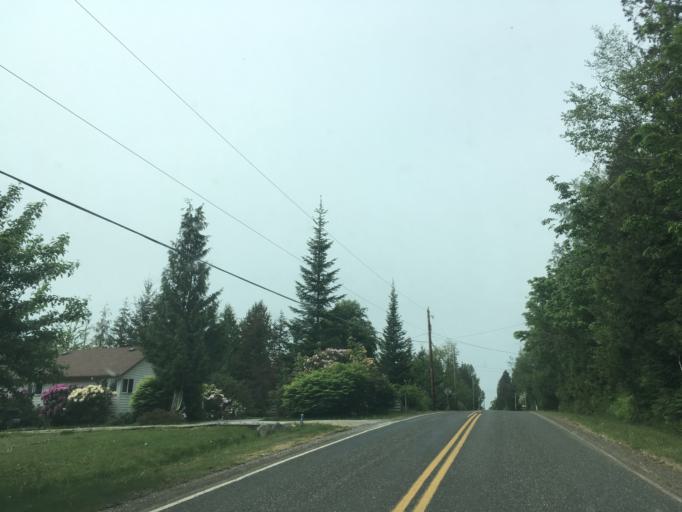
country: US
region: Washington
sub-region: Whatcom County
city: Geneva
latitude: 48.8187
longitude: -122.4061
